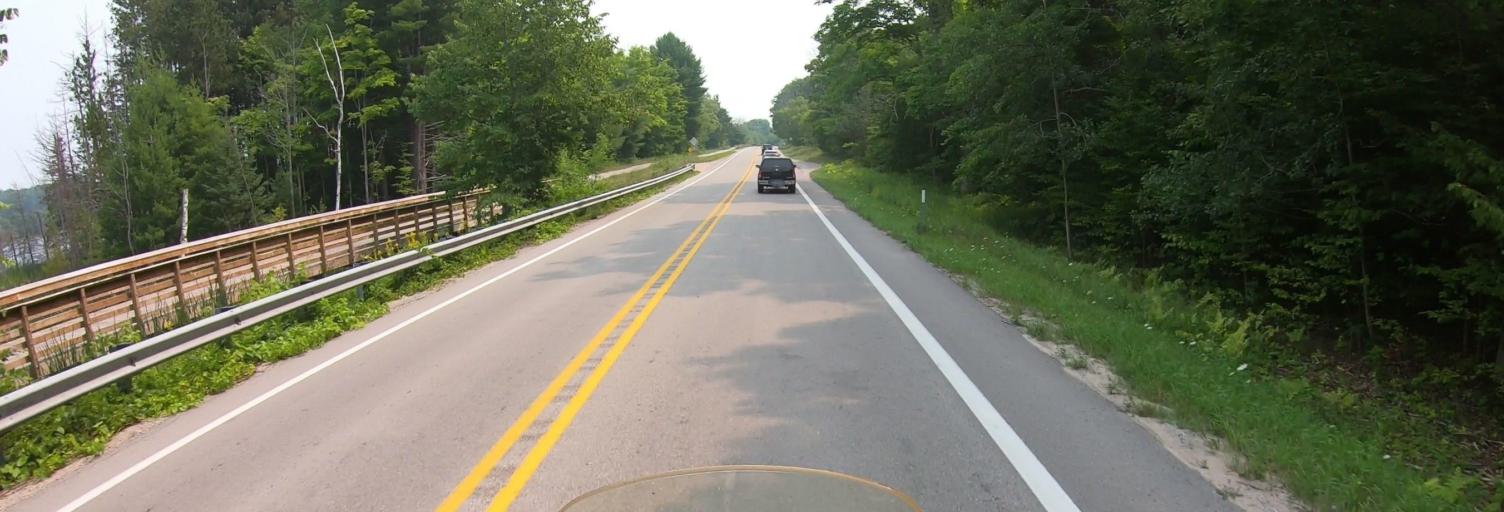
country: US
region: Michigan
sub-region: Leelanau County
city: Leland
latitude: 44.9331
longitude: -85.9066
